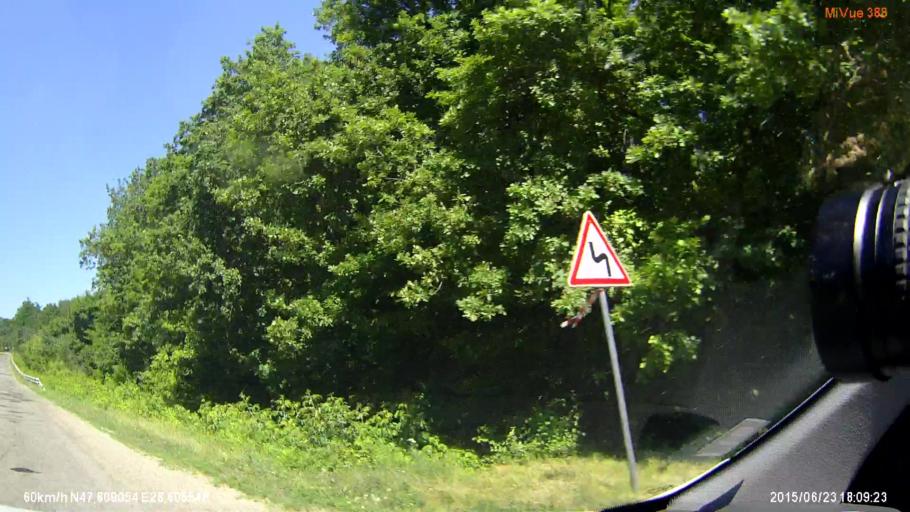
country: MD
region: Soldanesti
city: Soldanesti
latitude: 47.8090
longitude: 28.6062
